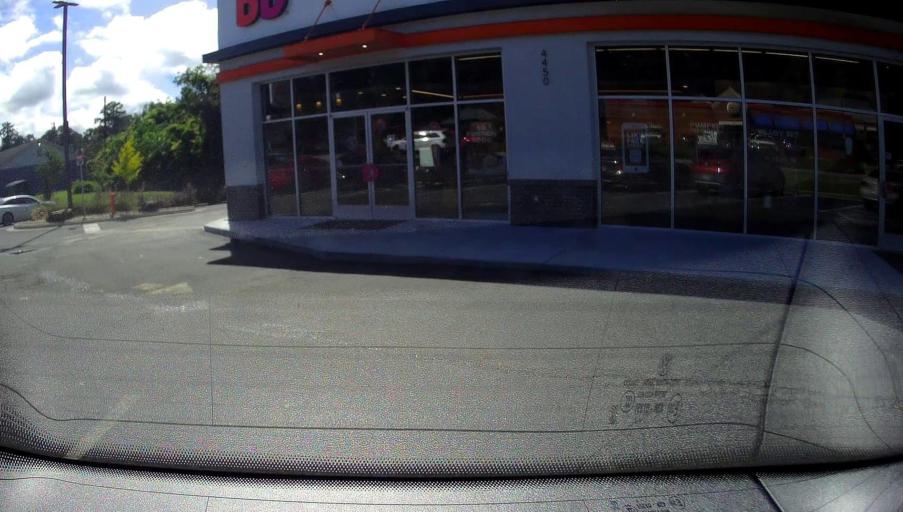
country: US
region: Georgia
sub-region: Bibb County
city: Macon
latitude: 32.8698
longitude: -83.7014
